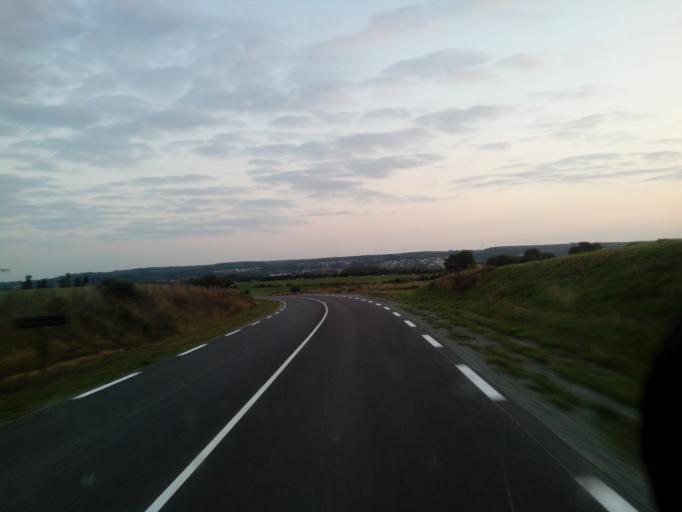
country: FR
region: Brittany
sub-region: Departement d'Ille-et-Vilaine
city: Bedee
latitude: 48.1573
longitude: -1.9464
